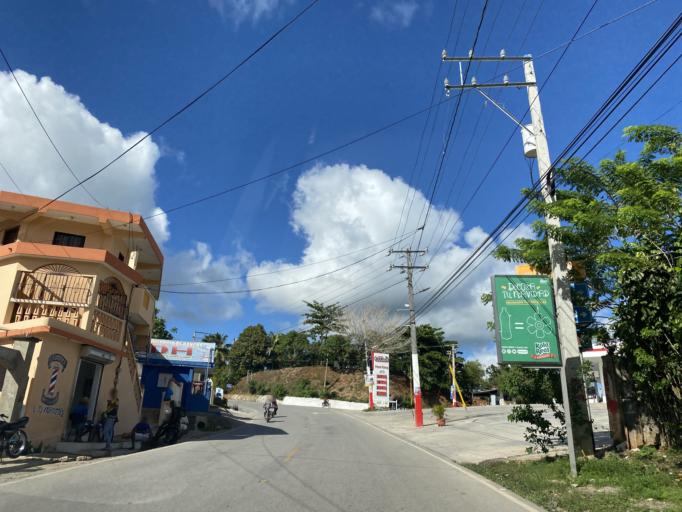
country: DO
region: Samana
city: Samana
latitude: 19.2120
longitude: -69.3555
